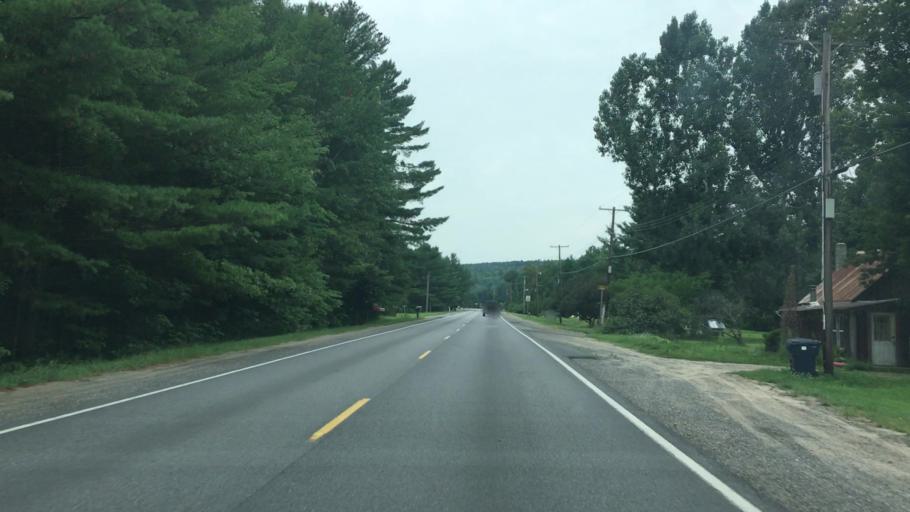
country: US
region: New York
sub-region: Clinton County
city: Peru
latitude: 44.5215
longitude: -73.5758
